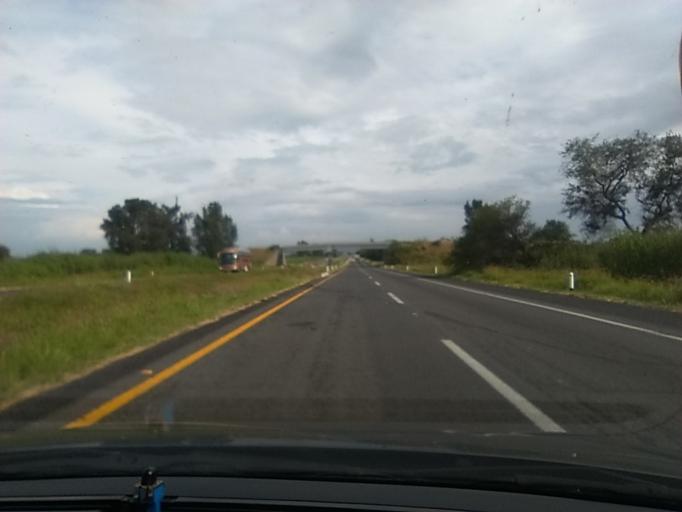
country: MX
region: Jalisco
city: La Barca
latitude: 20.3173
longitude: -102.5015
